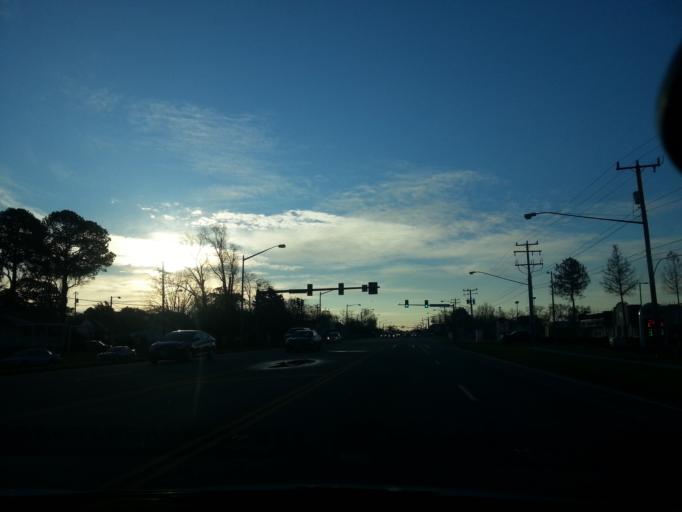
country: US
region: Virginia
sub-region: City of Norfolk
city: Norfolk
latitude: 36.8977
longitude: -76.2258
